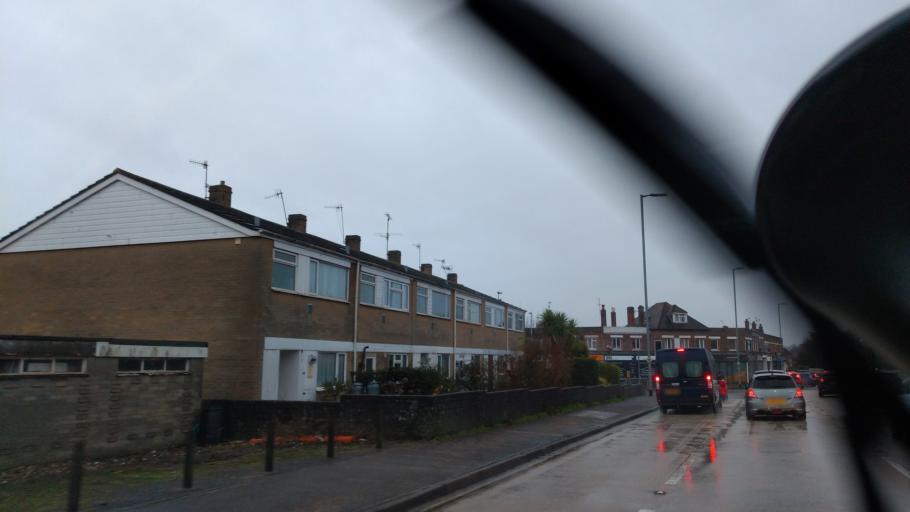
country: GB
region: England
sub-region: West Sussex
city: Broadwater
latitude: 50.8342
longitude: -0.3663
